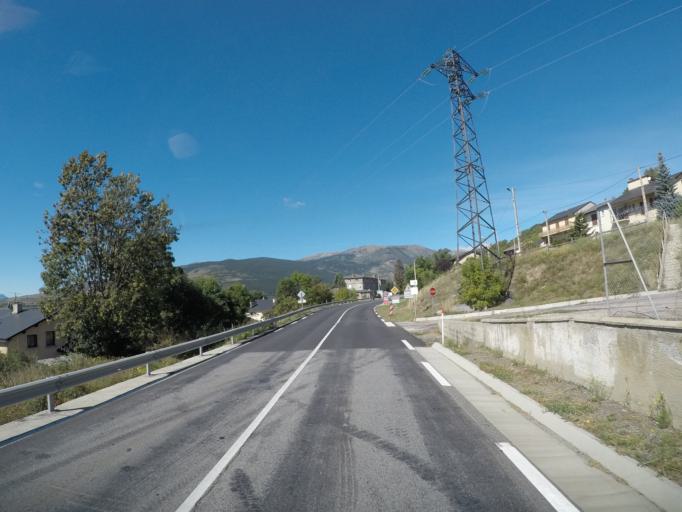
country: ES
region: Catalonia
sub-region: Provincia de Girona
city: Puigcerda
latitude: 42.4583
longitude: 1.9217
